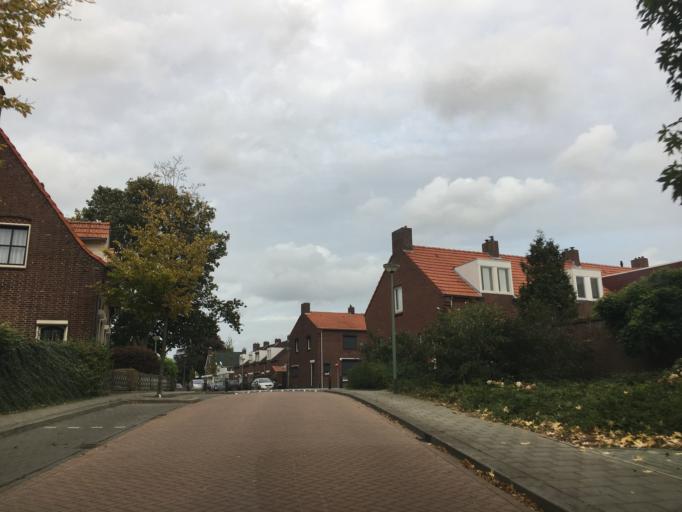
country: NL
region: Limburg
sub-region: Gemeente Roermond
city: Roermond
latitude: 51.1767
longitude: 5.9998
